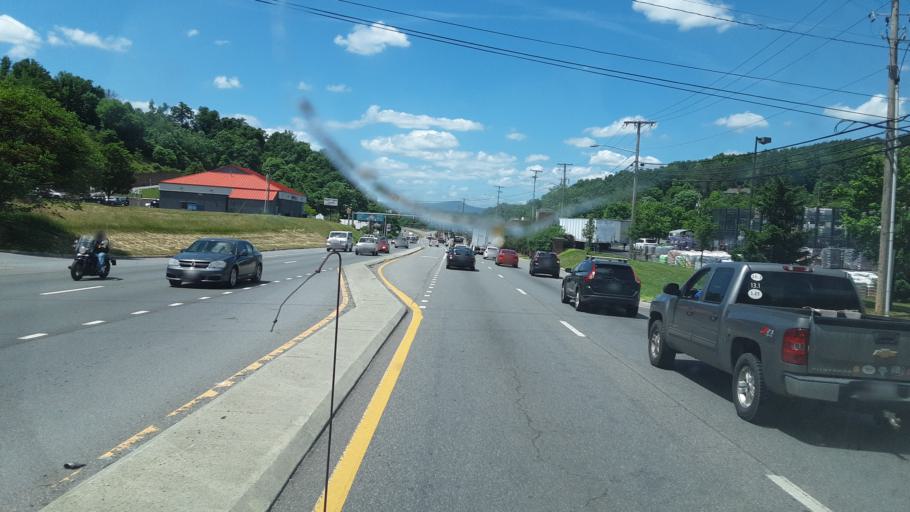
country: US
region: Virginia
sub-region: Roanoke County
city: Narrows
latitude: 37.2240
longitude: -79.9686
